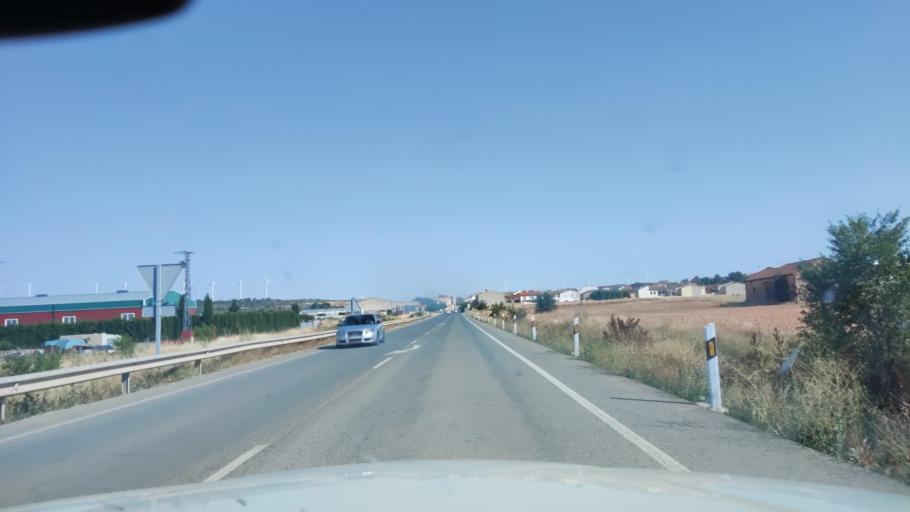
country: ES
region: Castille-La Mancha
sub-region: Provincia de Albacete
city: Pozo-Canada
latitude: 38.8091
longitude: -1.7370
